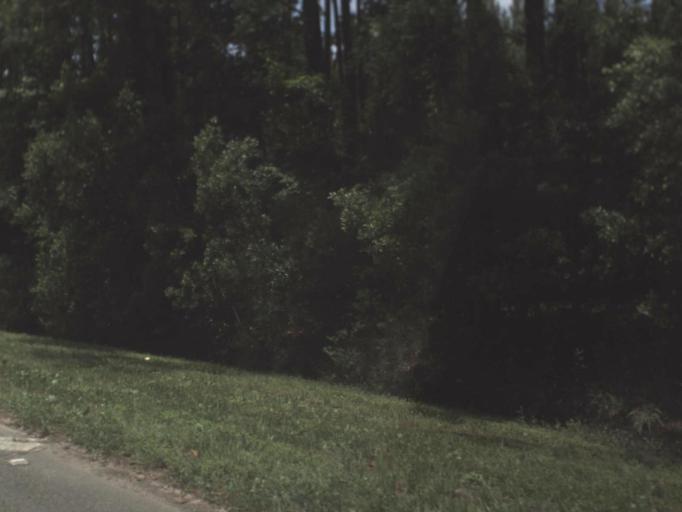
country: US
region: Florida
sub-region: Nassau County
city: Yulee
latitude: 30.6477
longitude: -81.6199
